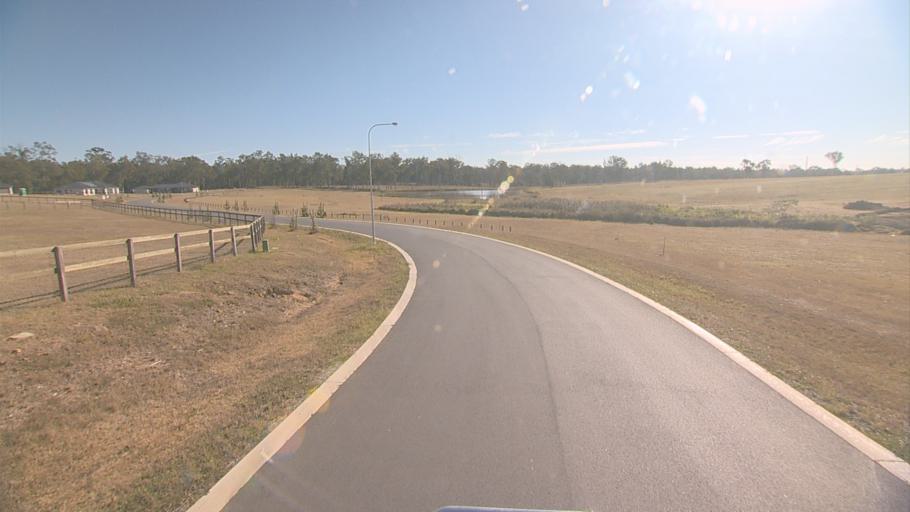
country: AU
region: Queensland
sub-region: Logan
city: North Maclean
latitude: -27.8107
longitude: 152.9959
